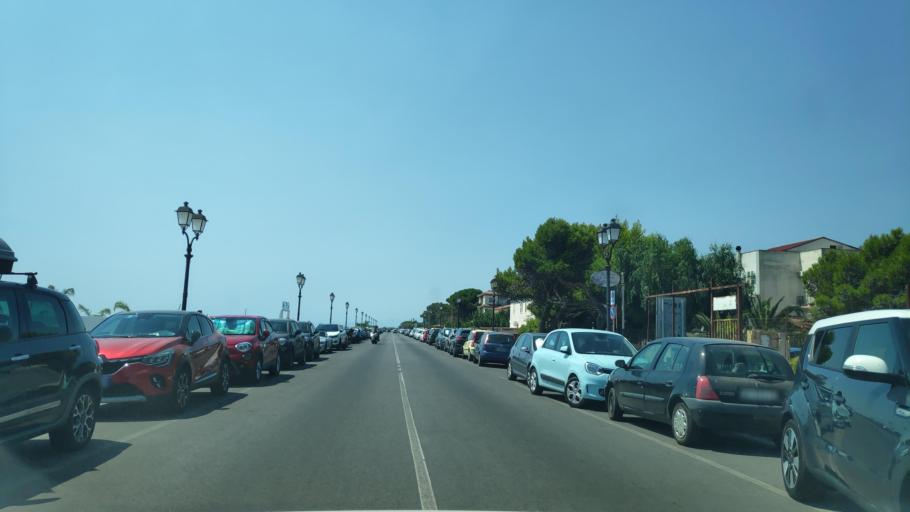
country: IT
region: Calabria
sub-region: Provincia di Reggio Calabria
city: Siderno
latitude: 38.2728
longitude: 16.3048
